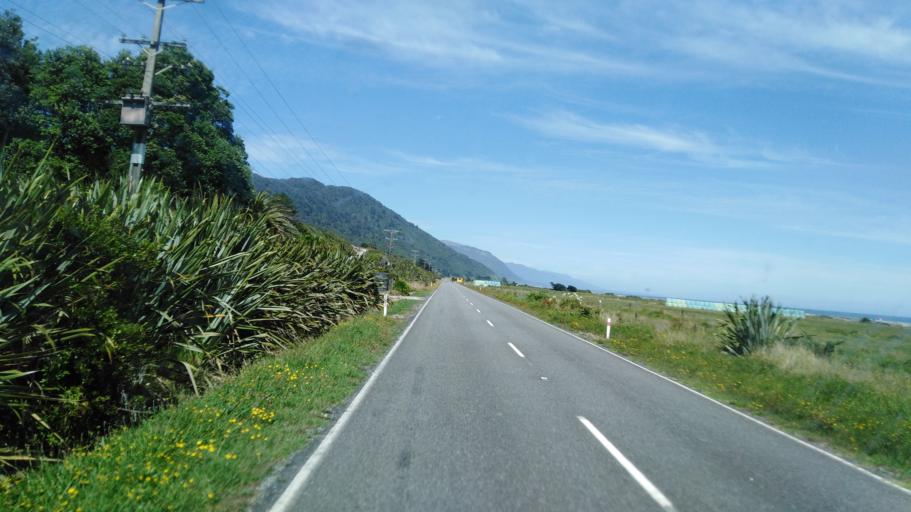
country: NZ
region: West Coast
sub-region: Buller District
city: Westport
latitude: -41.5429
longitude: 171.9271
